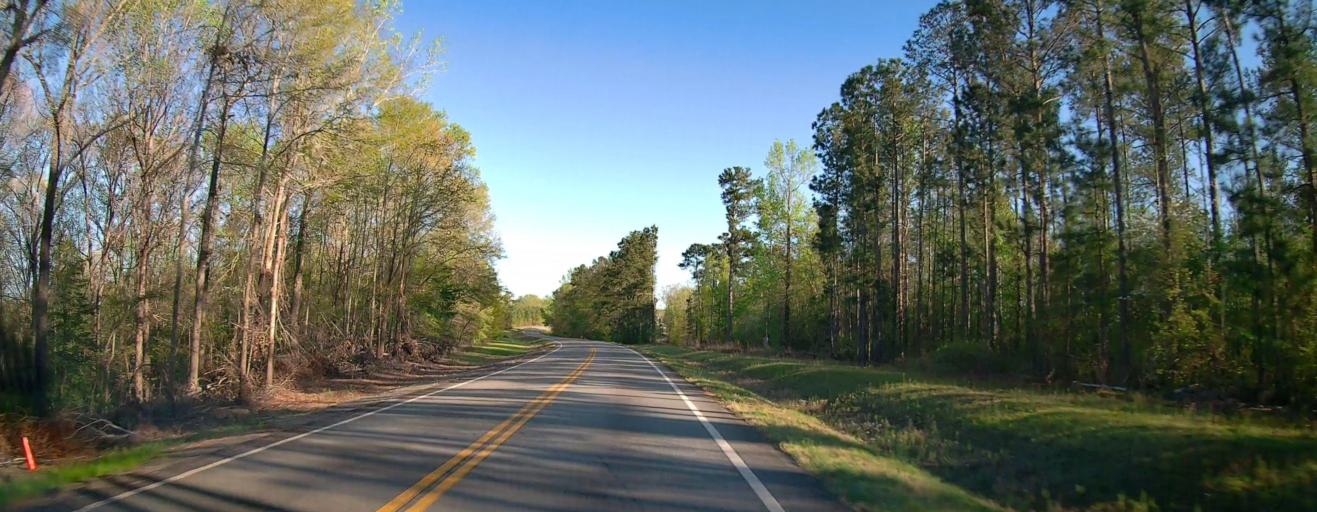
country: US
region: Georgia
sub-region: Wilkinson County
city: Irwinton
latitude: 32.9114
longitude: -83.1246
